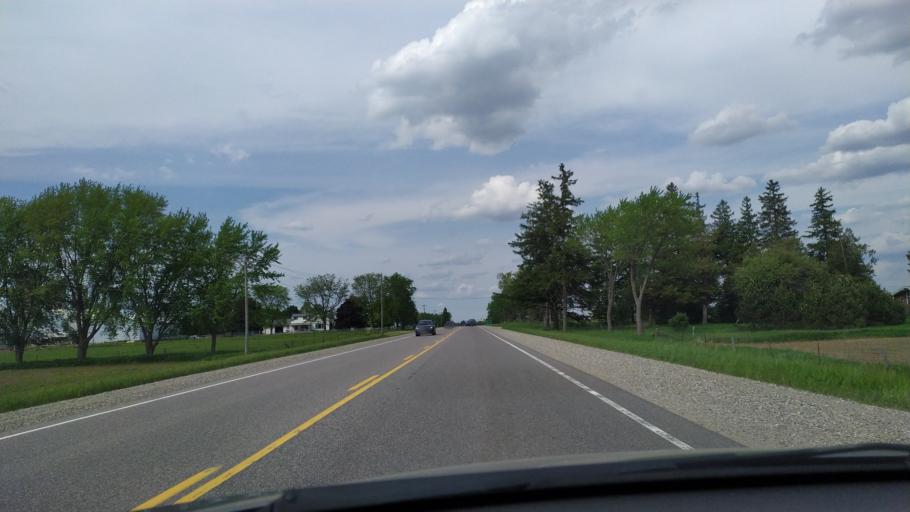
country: CA
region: Ontario
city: Stratford
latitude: 43.3020
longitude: -81.0410
